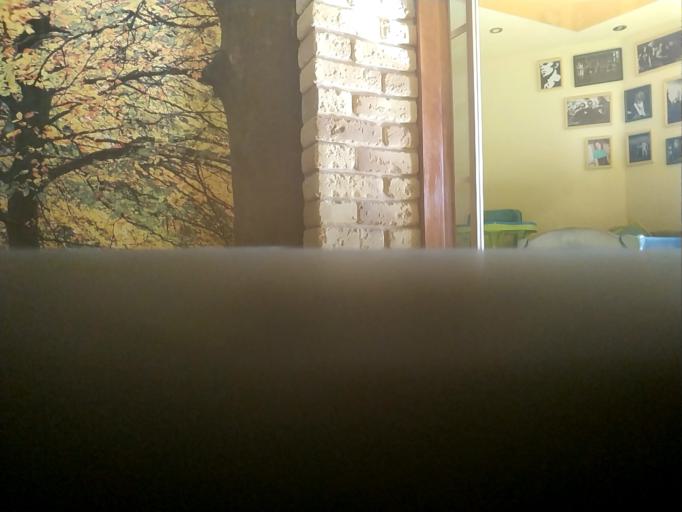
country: RU
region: Smolensk
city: Temkino
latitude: 54.9769
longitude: 34.9464
